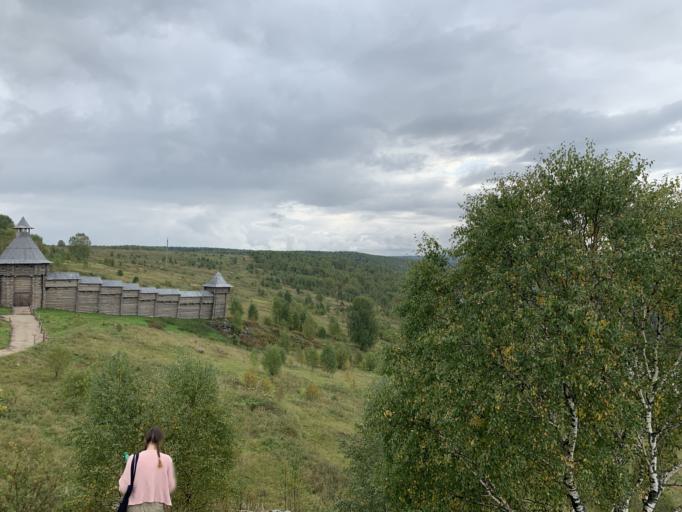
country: RU
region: Perm
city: Gubakha
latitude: 58.8696
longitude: 57.6268
